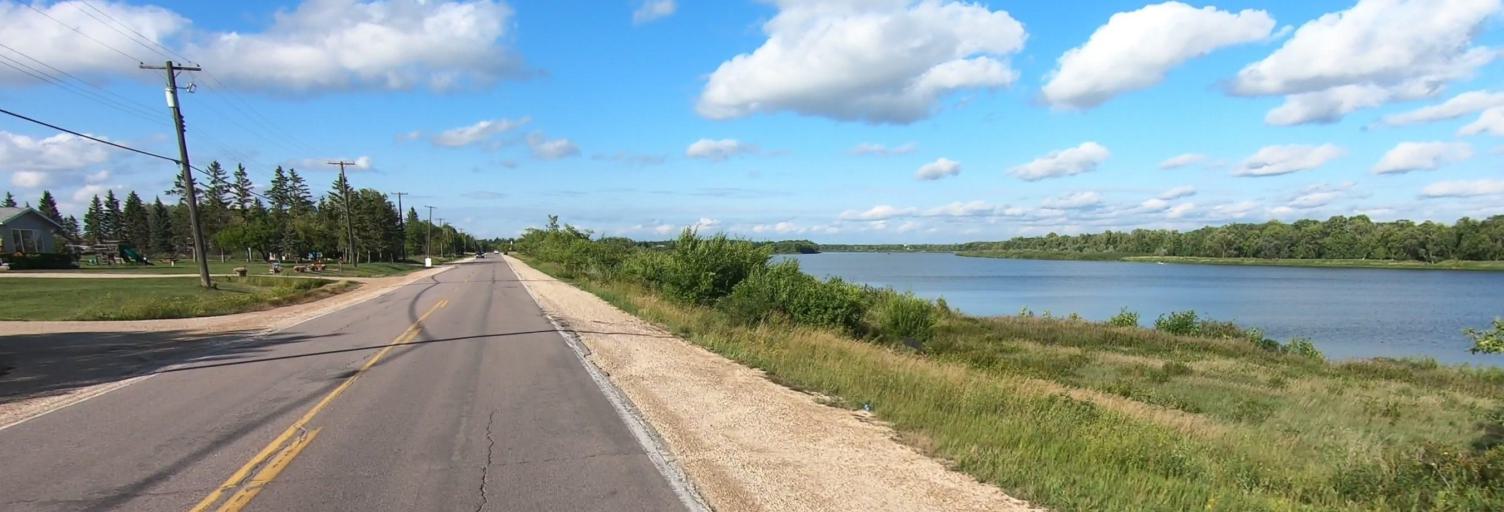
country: CA
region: Manitoba
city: Selkirk
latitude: 50.1711
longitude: -96.8616
